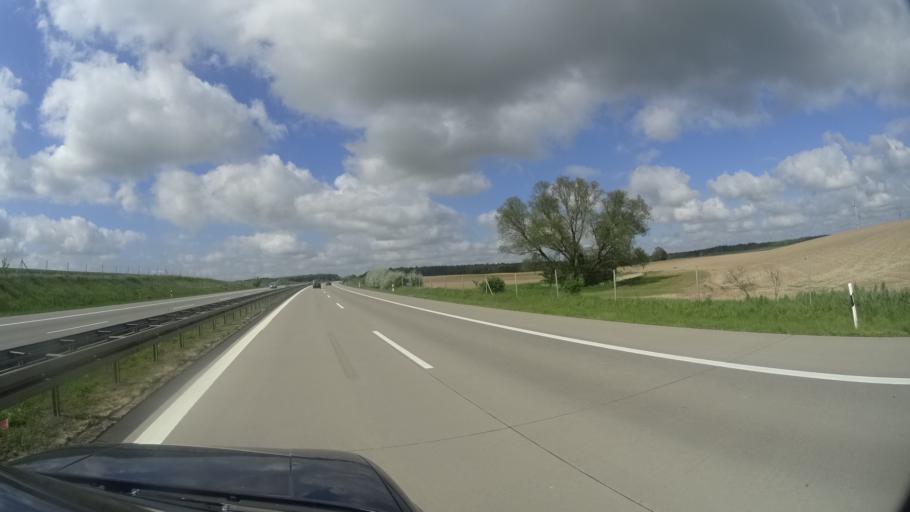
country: DE
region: Mecklenburg-Vorpommern
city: Kavelstorf
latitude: 53.9577
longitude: 12.1974
